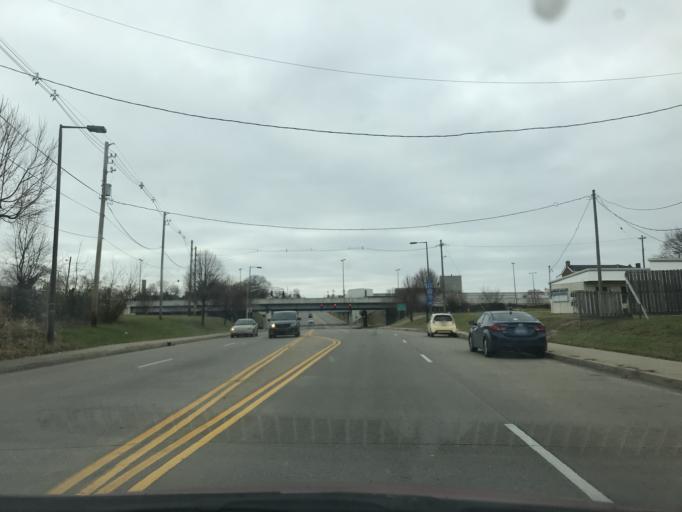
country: US
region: Kentucky
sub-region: Jefferson County
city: Louisville
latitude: 38.2356
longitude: -85.7660
